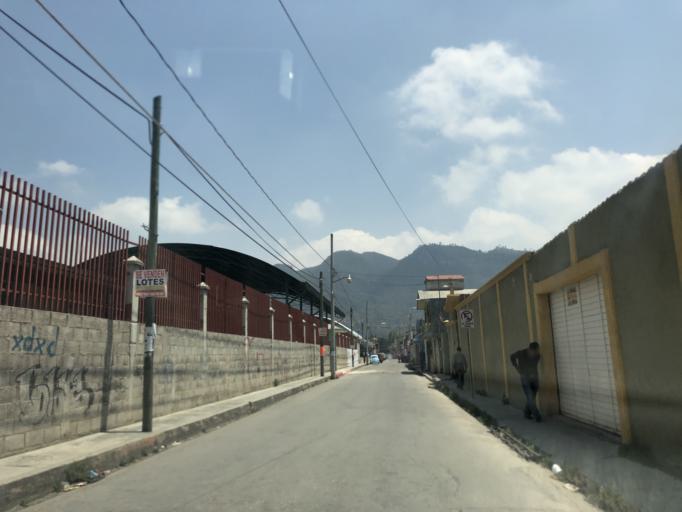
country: MX
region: Chiapas
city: San Cristobal de las Casas
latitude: 16.7191
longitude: -92.6432
